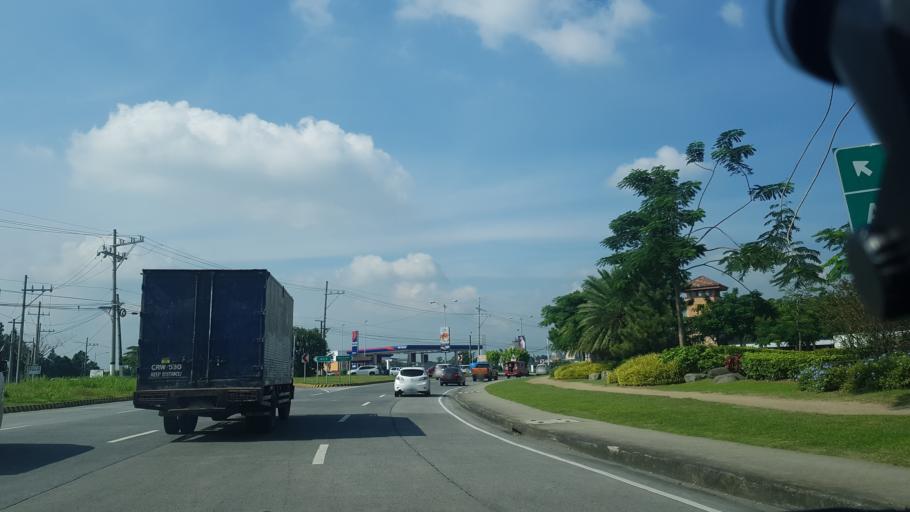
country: PH
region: Calabarzon
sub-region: Province of Laguna
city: San Pedro
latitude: 14.3758
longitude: 121.0127
